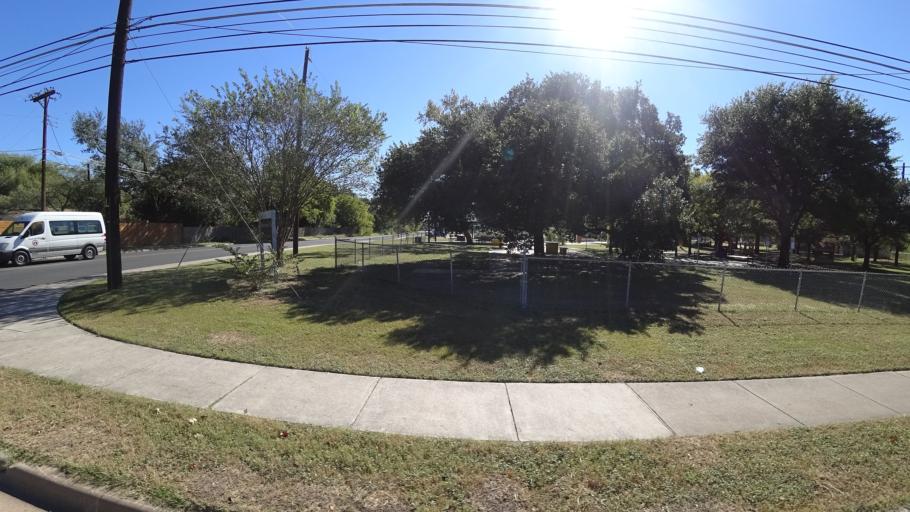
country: US
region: Texas
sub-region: Travis County
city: Austin
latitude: 30.3056
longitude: -97.6977
